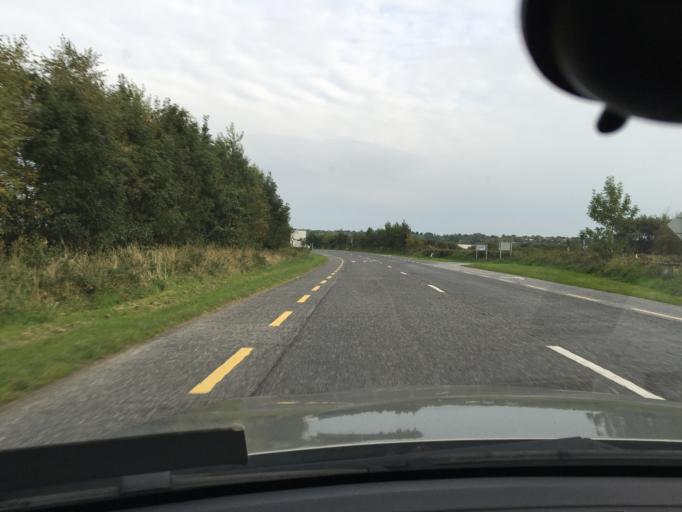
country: IE
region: Leinster
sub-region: An Longfort
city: Longford
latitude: 53.7241
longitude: -7.8230
